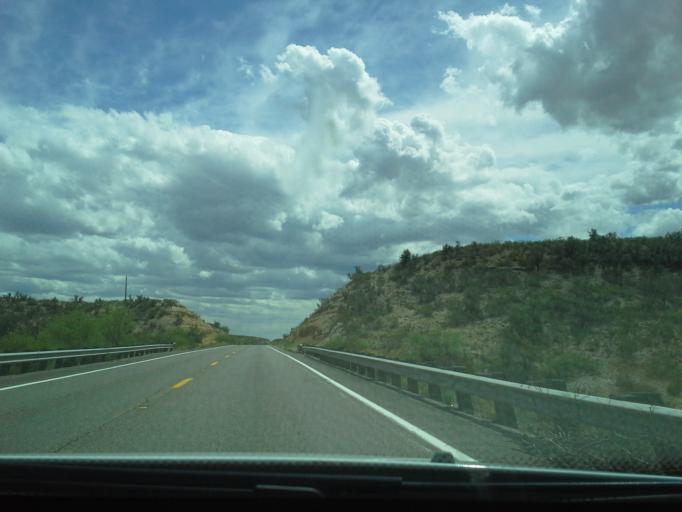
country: US
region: Arizona
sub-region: Graham County
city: Bylas
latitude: 33.2289
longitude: -110.2352
